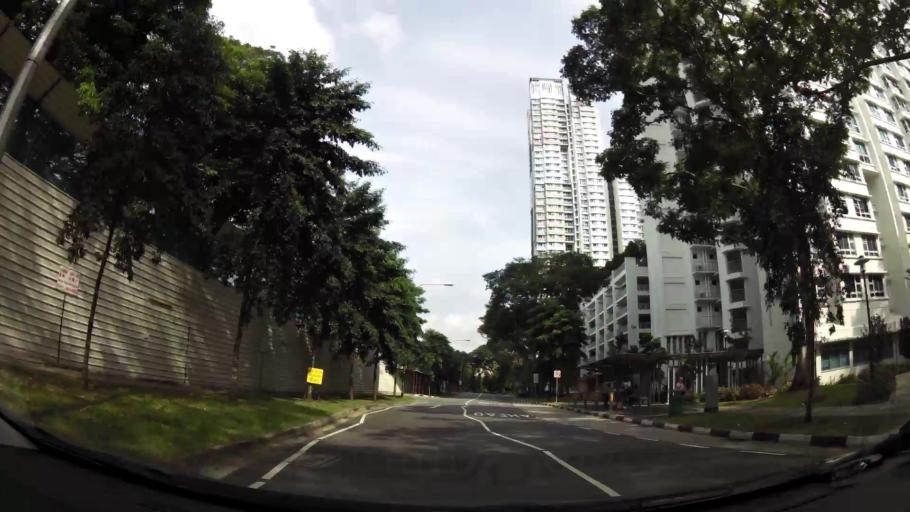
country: SG
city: Singapore
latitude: 1.3008
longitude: 103.7968
